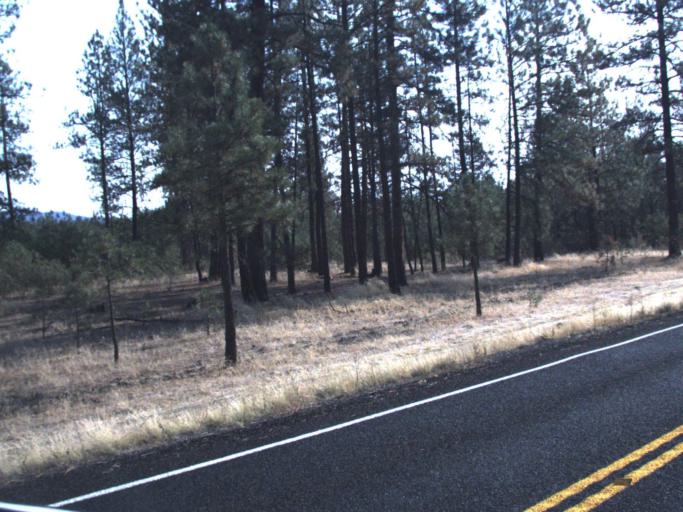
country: US
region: Washington
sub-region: Spokane County
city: Fairchild Air Force Base
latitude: 47.8403
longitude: -117.8356
